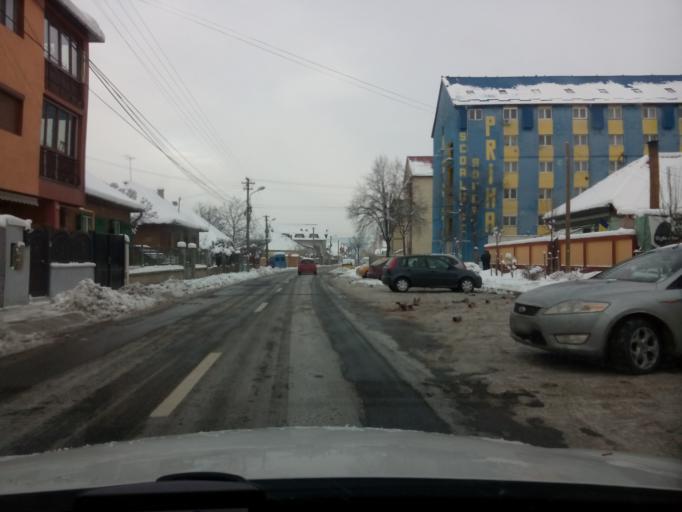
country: RO
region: Sibiu
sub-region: Municipiul Sibiu
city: Sibiu
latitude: 45.7838
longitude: 24.1653
